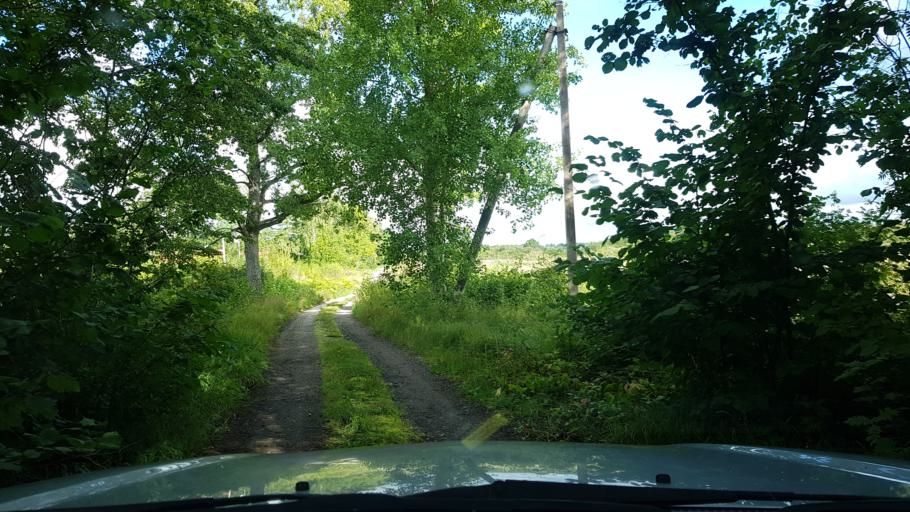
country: EE
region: Harju
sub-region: Rae vald
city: Vaida
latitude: 59.2678
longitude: 25.0282
